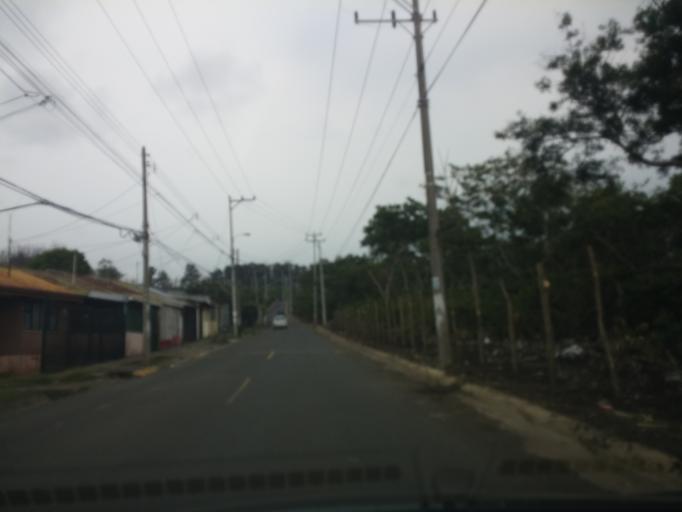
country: CR
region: Heredia
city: Llorente
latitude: 9.9839
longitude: -84.1479
